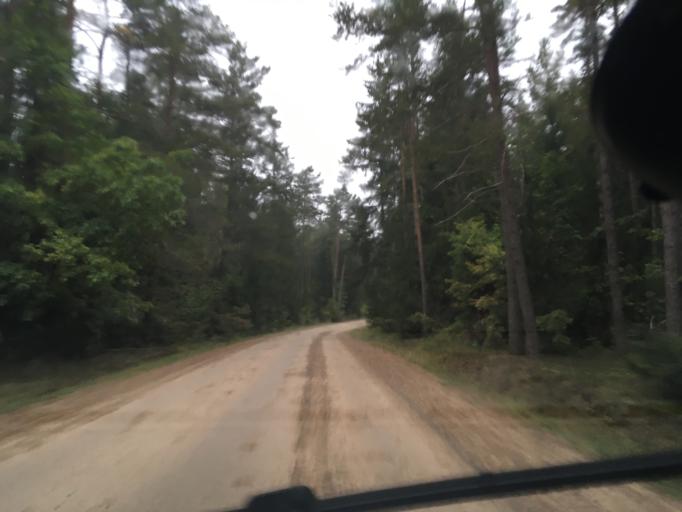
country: LV
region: Kuldigas Rajons
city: Kuldiga
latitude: 56.9904
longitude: 21.9742
